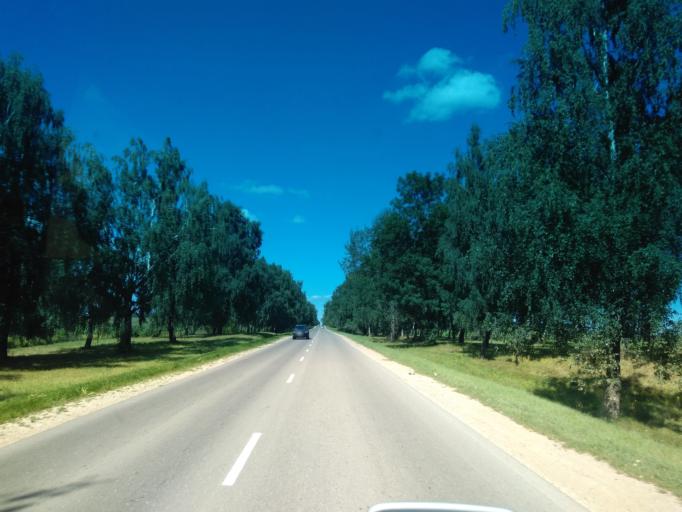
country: BY
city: Fanipol
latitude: 53.6995
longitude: 27.3544
